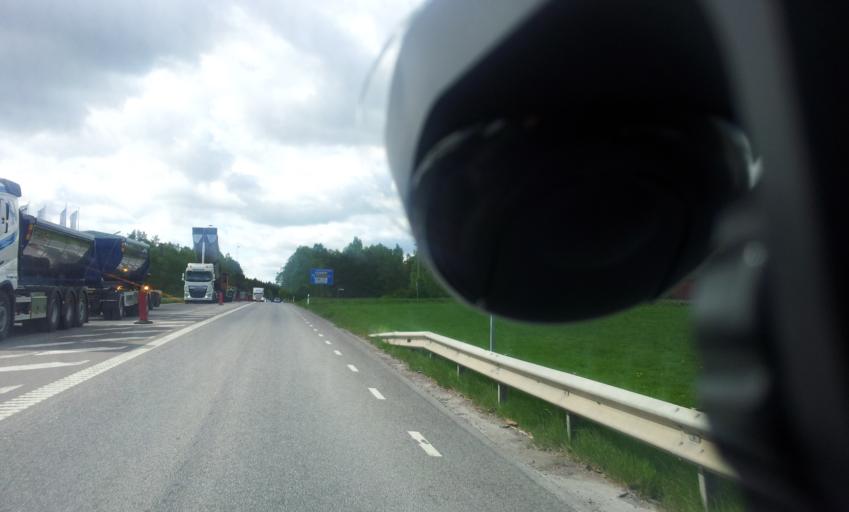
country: SE
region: Kalmar
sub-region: Monsteras Kommun
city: Moensteras
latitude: 57.0258
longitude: 16.4308
